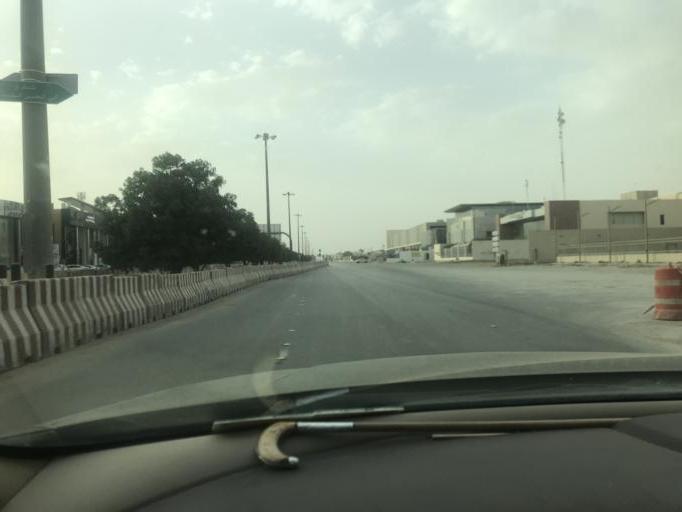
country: SA
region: Ar Riyad
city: Riyadh
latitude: 24.7871
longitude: 46.6598
